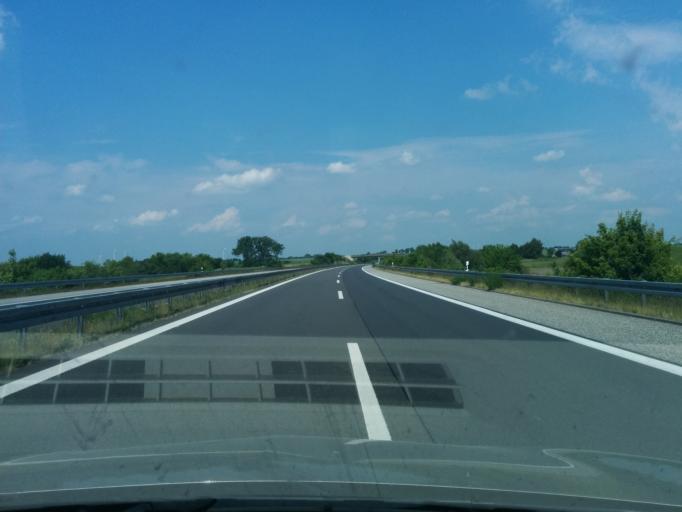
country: DE
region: Brandenburg
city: Grunow
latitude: 53.2906
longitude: 13.9865
